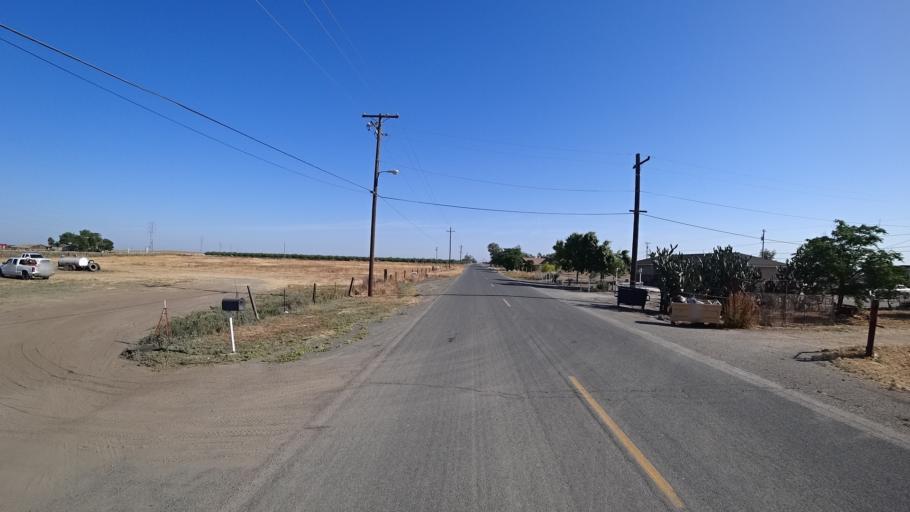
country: US
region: California
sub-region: Kings County
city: Corcoran
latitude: 36.1217
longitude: -119.5633
